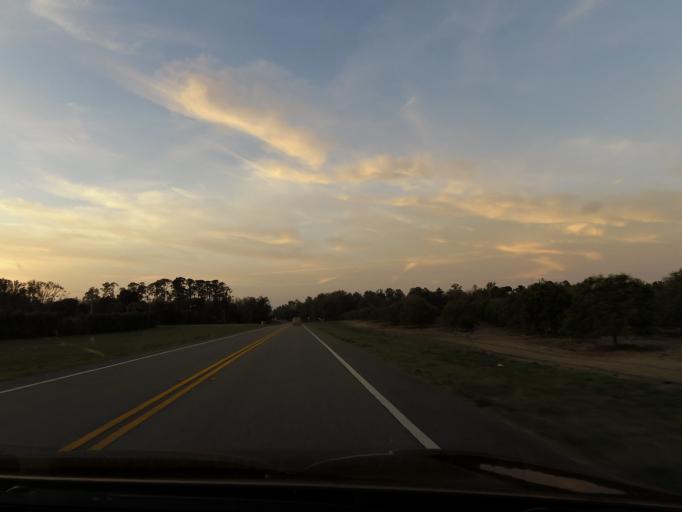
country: US
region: Florida
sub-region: Volusia County
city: De Leon Springs
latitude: 29.1612
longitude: -81.2965
